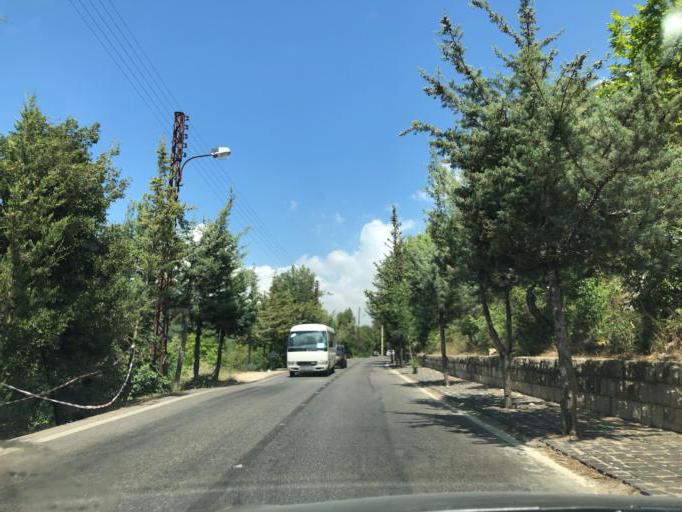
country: LB
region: Mont-Liban
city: Beit ed Dine
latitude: 33.6963
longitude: 35.5848
